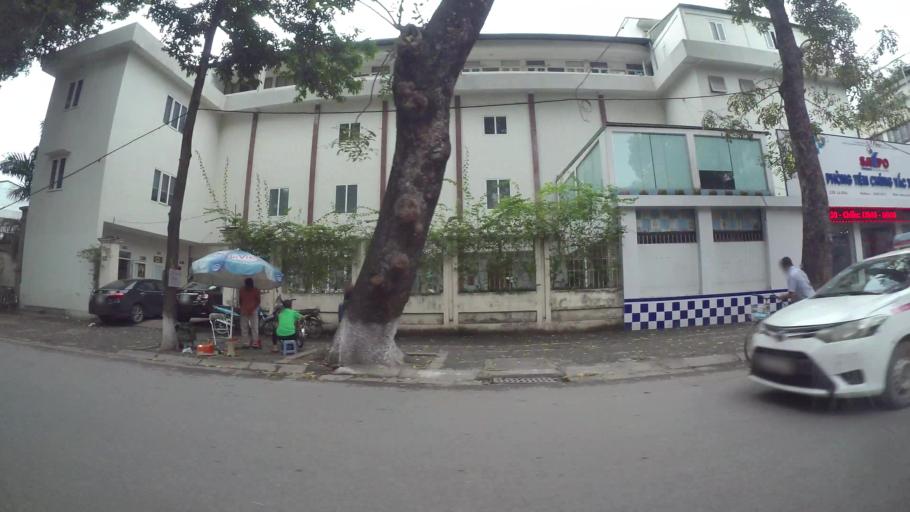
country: VN
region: Ha Noi
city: Hai BaTrung
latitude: 21.0116
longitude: 105.8592
